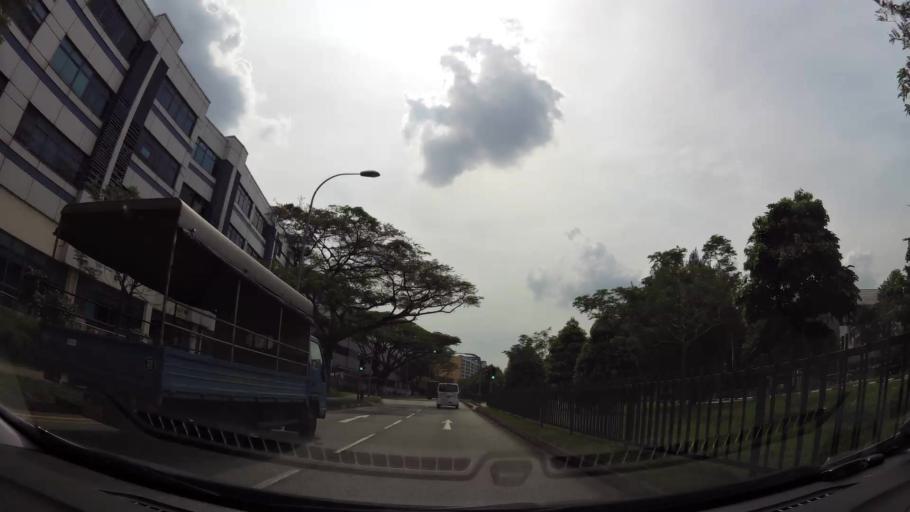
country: MY
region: Johor
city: Johor Bahru
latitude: 1.4544
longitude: 103.7959
